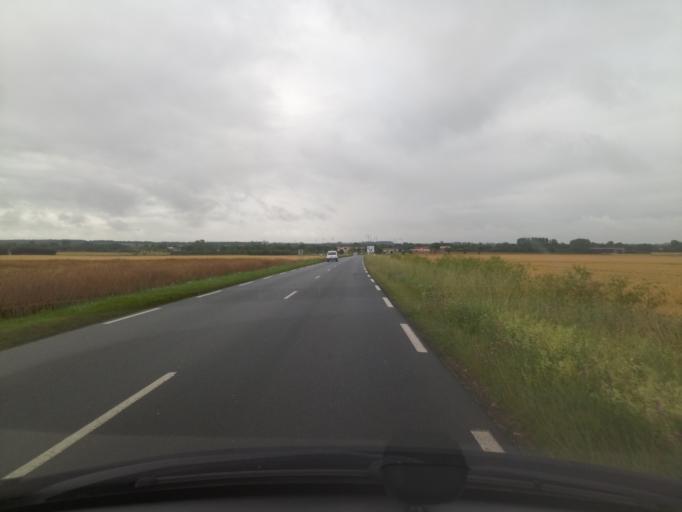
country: FR
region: Poitou-Charentes
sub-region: Departement de la Charente-Maritime
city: Saint-Jean-de-Liversay
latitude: 46.1985
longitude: -0.8703
